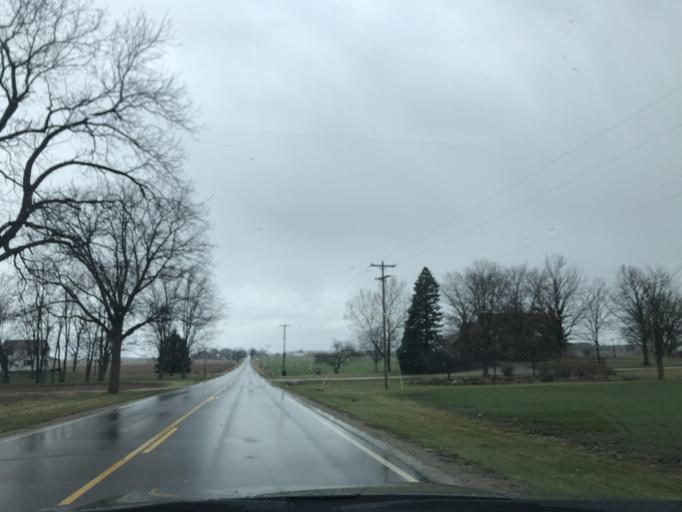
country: US
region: Michigan
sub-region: Clinton County
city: Fowler
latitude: 42.9502
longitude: -84.6609
